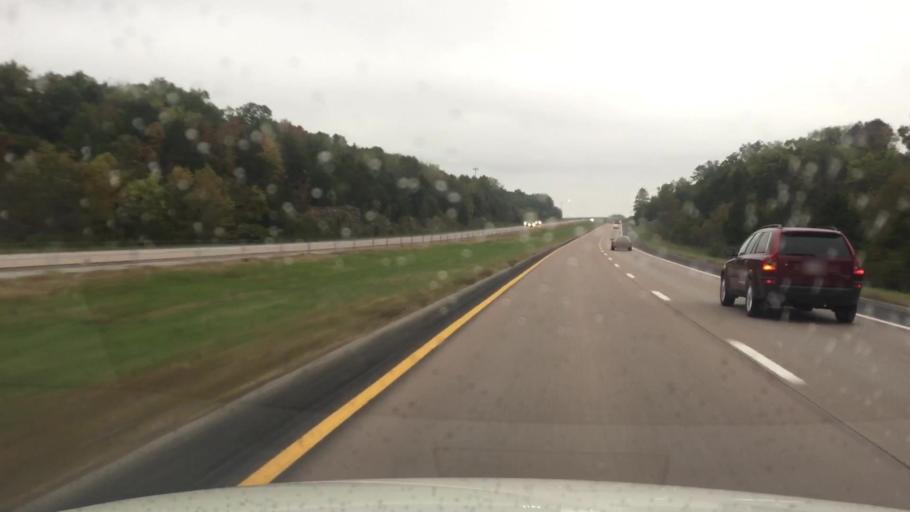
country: US
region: Missouri
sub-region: Boone County
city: Ashland
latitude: 38.8223
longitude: -92.2509
